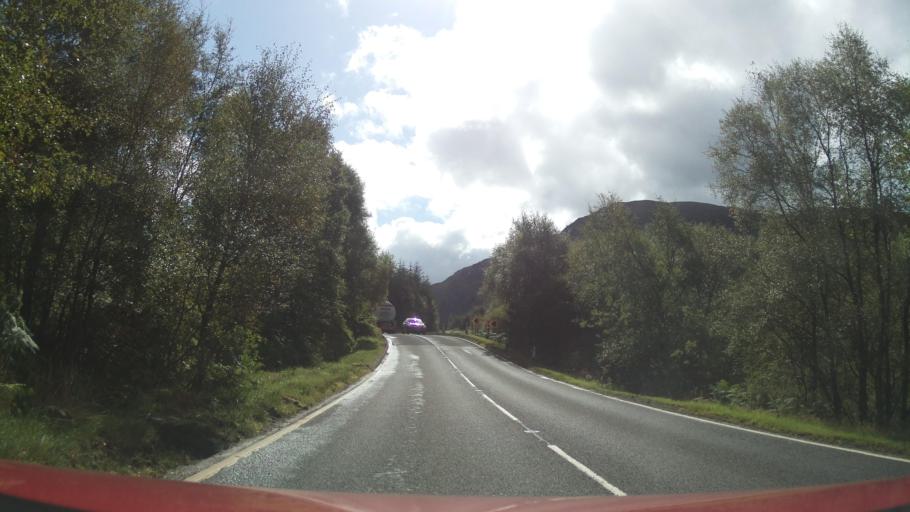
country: GB
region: Scotland
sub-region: Stirling
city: Callander
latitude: 56.4171
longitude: -4.3347
